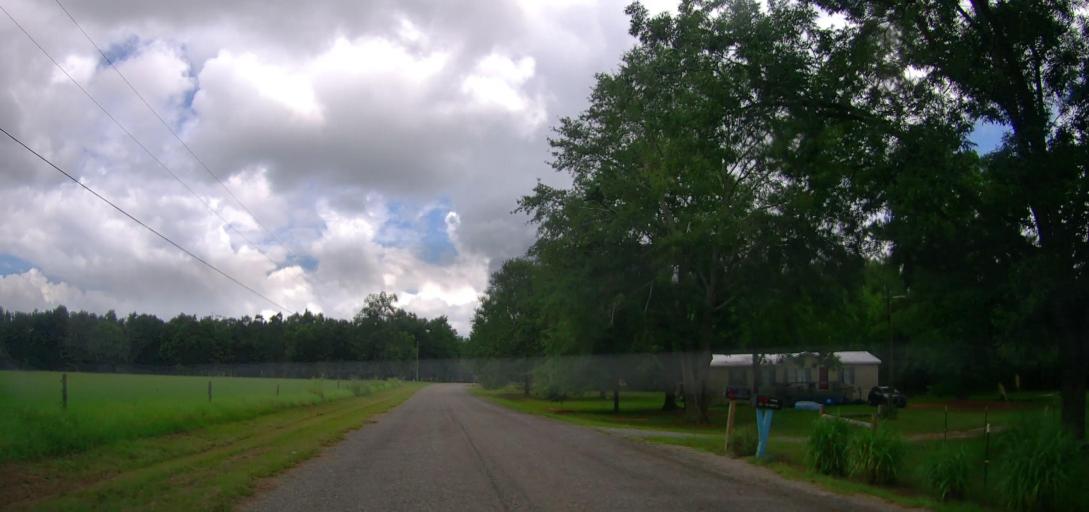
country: US
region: Georgia
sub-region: Pulaski County
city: Hawkinsville
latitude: 32.3170
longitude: -83.5328
